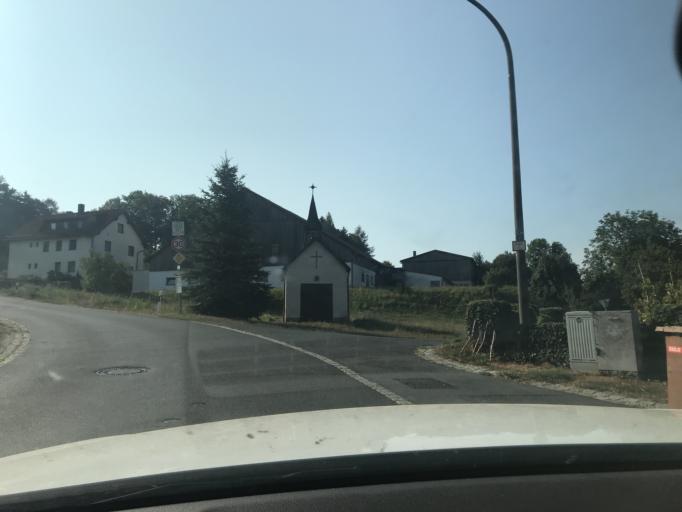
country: DE
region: Bavaria
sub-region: Upper Franconia
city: Pegnitz
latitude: 49.7421
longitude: 11.5645
